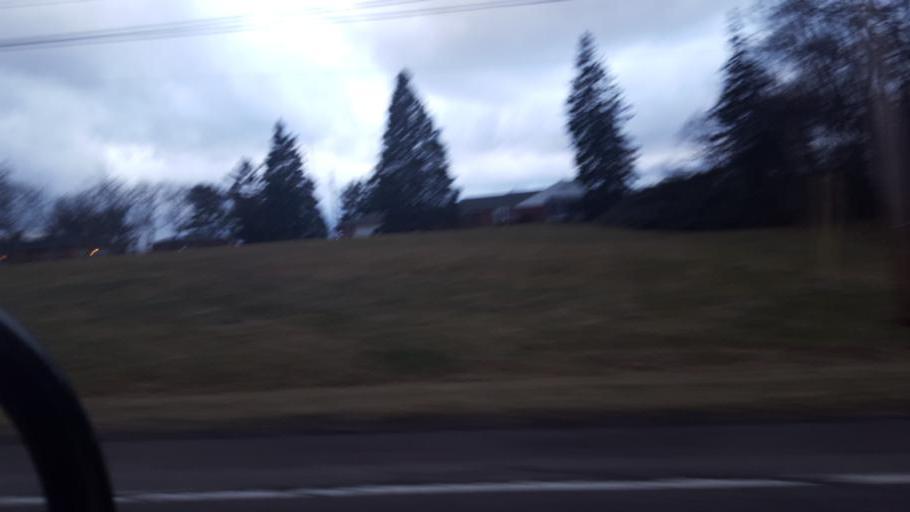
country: US
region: Ohio
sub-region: Richland County
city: Mansfield
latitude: 40.7304
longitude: -82.5514
